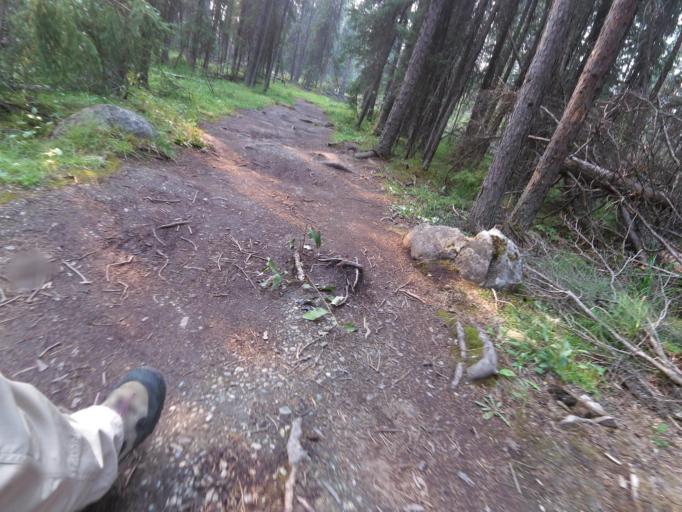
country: CA
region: Alberta
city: Jasper Park Lodge
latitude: 52.8851
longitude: -118.0651
